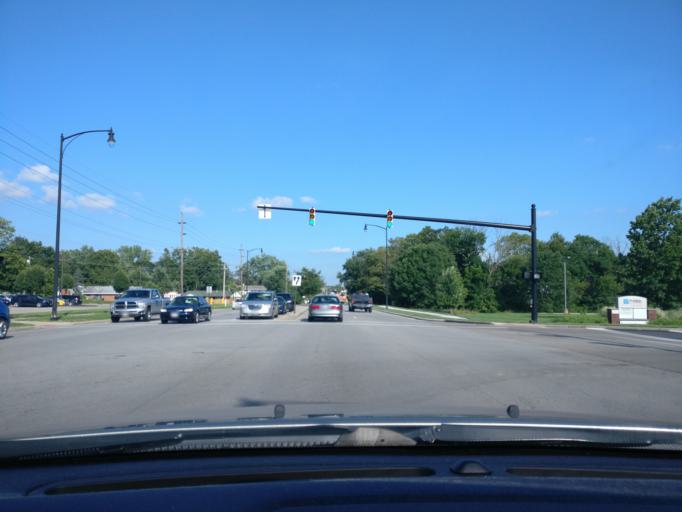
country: US
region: Ohio
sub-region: Warren County
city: Springboro
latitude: 39.5587
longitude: -84.2397
